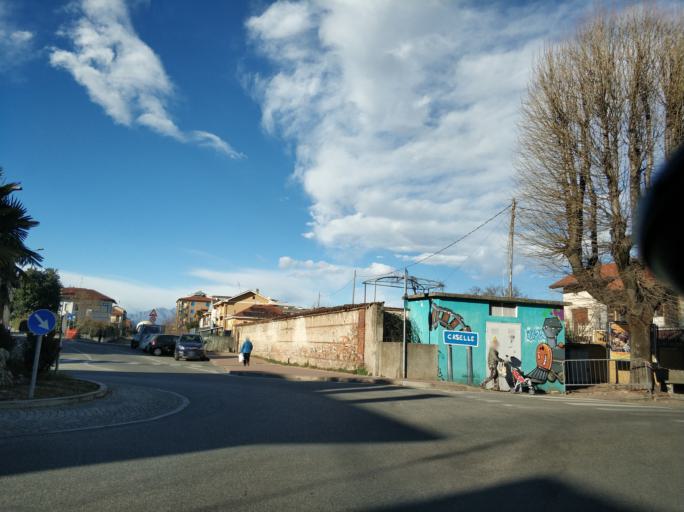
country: IT
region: Piedmont
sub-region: Provincia di Torino
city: Caselle Torinese
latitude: 45.1774
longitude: 7.6443
